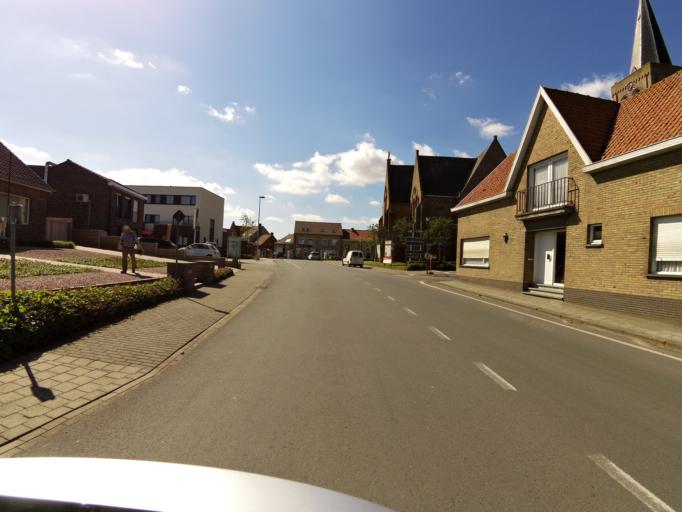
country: BE
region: Flanders
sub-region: Provincie West-Vlaanderen
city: Houthulst
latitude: 50.9979
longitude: 2.9042
